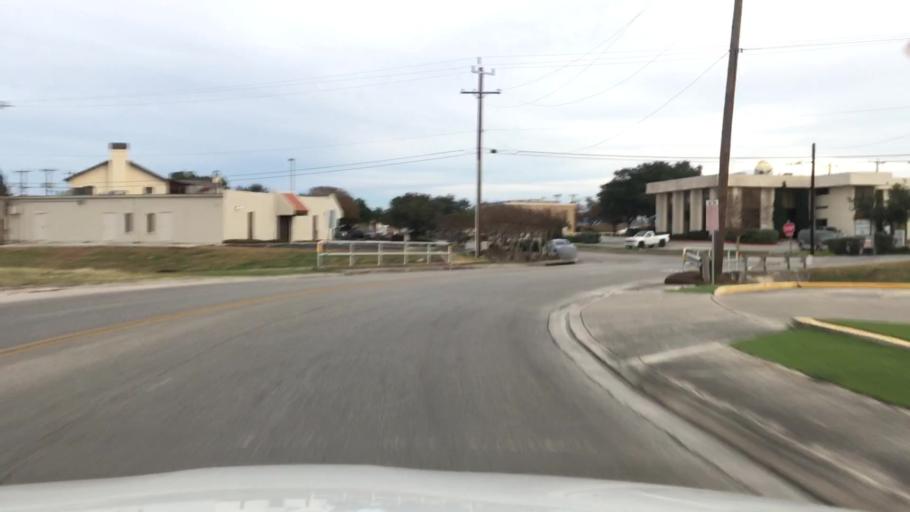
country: US
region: Texas
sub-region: Bexar County
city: Windcrest
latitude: 29.5117
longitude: -98.3907
